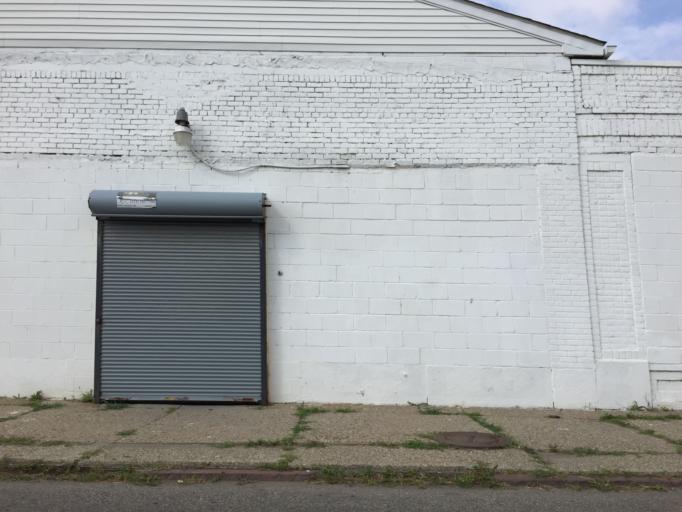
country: US
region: Michigan
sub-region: Wayne County
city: Hamtramck
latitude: 42.3644
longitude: -83.0400
